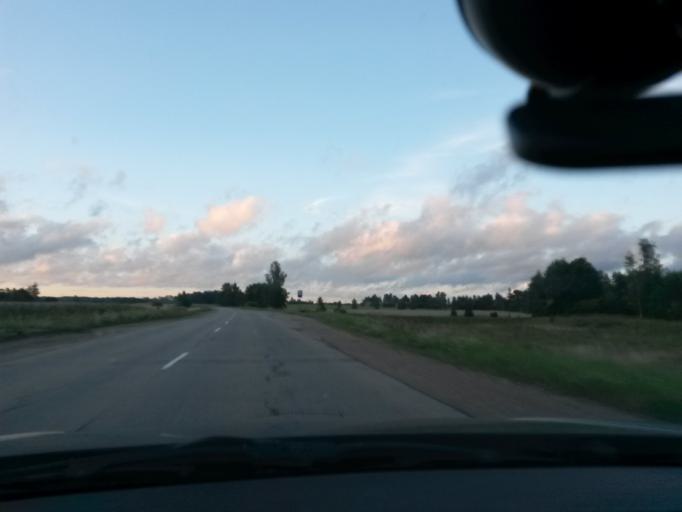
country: LV
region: Madonas Rajons
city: Madona
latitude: 56.7355
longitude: 26.0149
